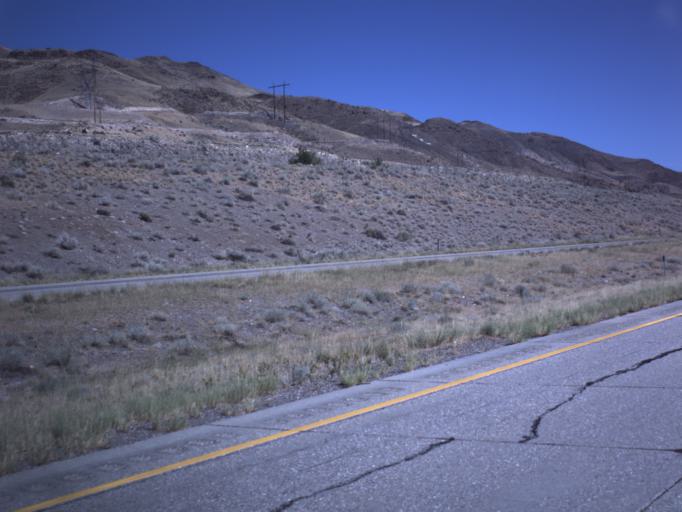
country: US
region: Utah
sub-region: Sevier County
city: Monroe
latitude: 38.6746
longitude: -112.1629
